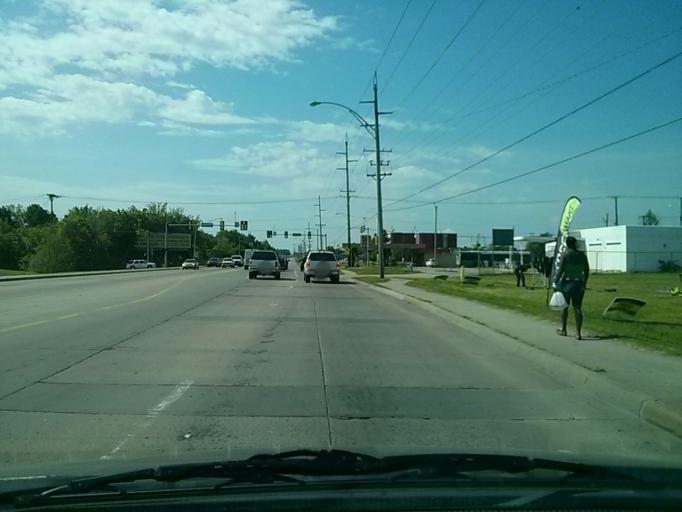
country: US
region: Oklahoma
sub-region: Tulsa County
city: Turley
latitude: 36.2071
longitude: -95.9757
